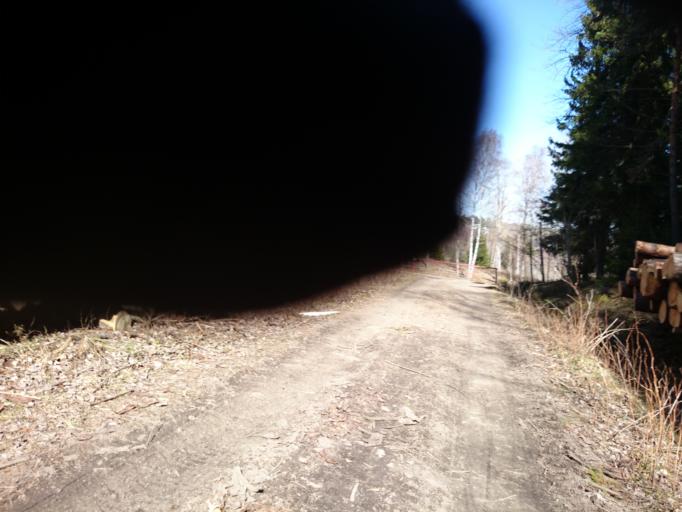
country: SE
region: Stockholm
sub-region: Botkyrka Kommun
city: Tullinge
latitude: 59.2326
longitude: 17.9097
